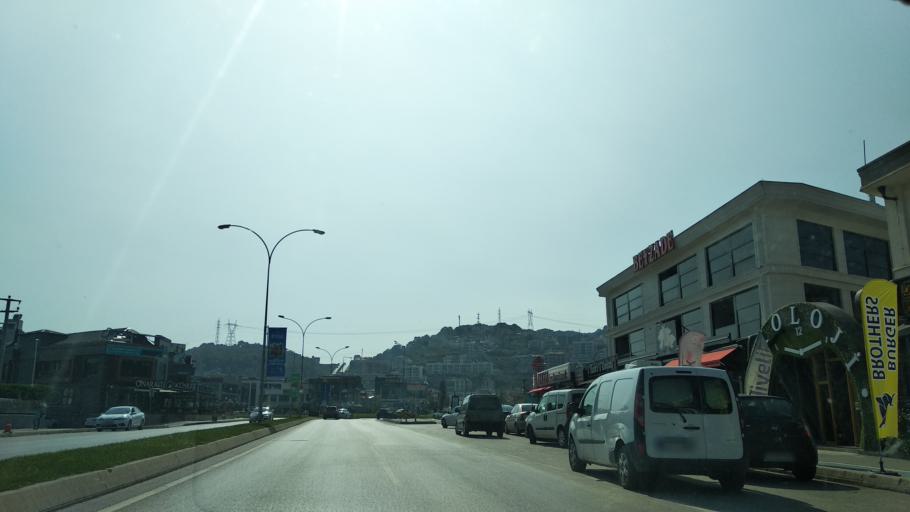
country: TR
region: Sakarya
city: Adapazari
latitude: 40.7616
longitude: 30.3630
